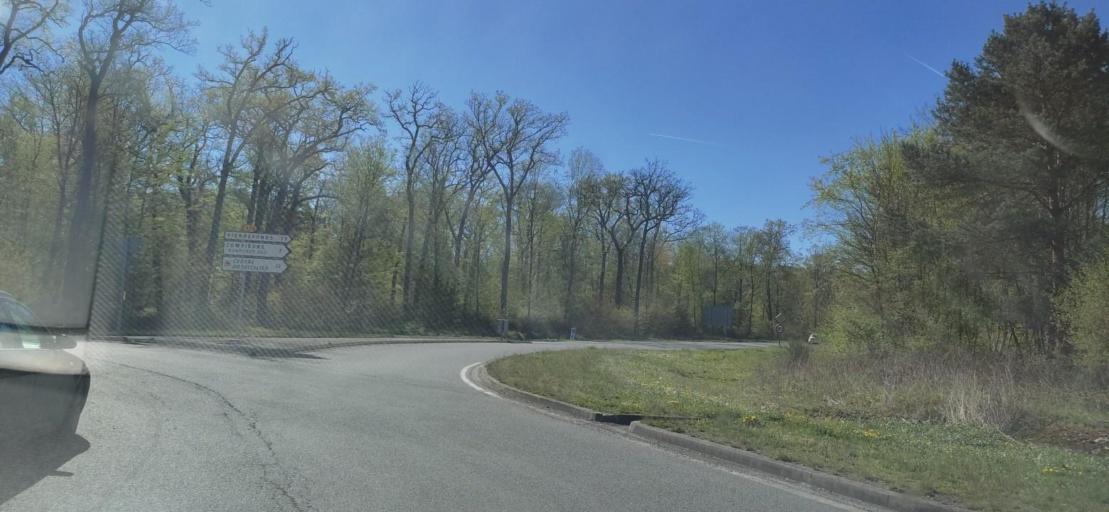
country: FR
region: Picardie
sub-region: Departement de l'Oise
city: Choisy-au-Bac
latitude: 49.4256
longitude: 2.8760
